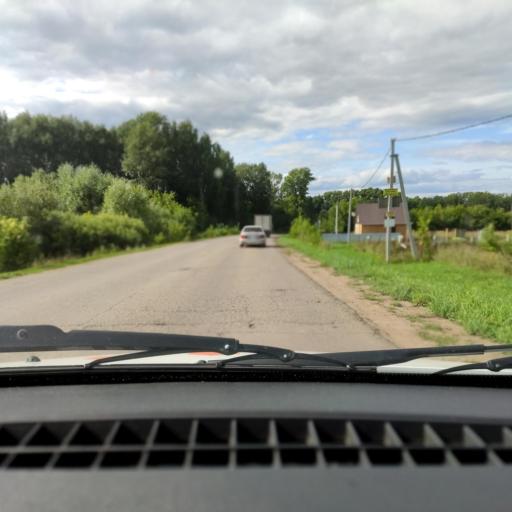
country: RU
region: Bashkortostan
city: Iglino
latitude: 54.8775
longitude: 56.5527
